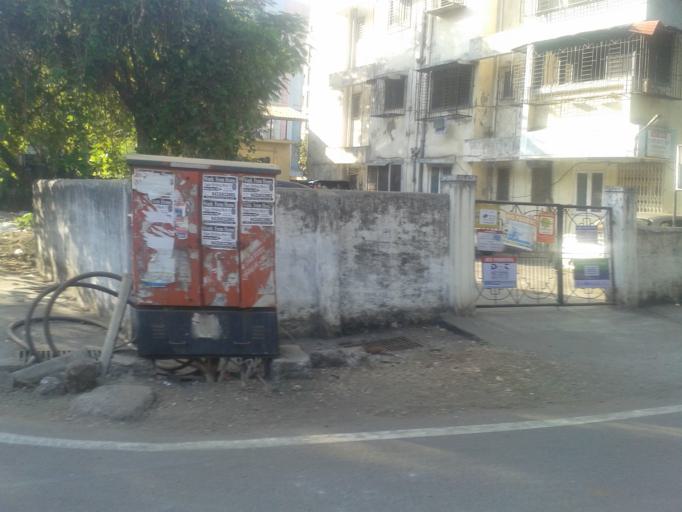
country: IN
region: Maharashtra
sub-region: Thane
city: Dombivli
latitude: 19.2055
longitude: 73.0867
